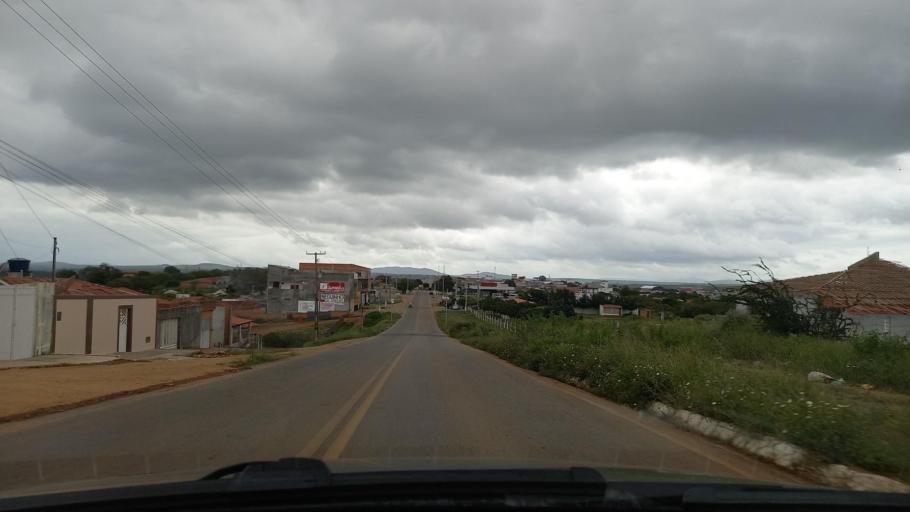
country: BR
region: Sergipe
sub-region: Caninde De Sao Francisco
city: Caninde de Sao Francisco
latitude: -9.6694
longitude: -37.7982
